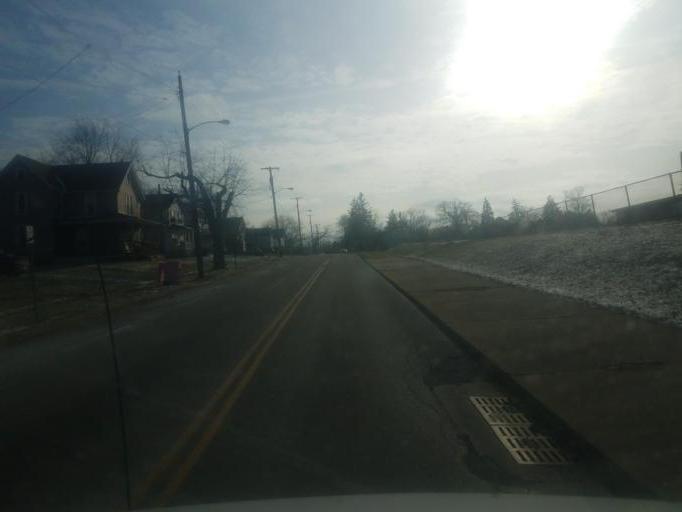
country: US
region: Ohio
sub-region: Richland County
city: Mansfield
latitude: 40.7536
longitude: -82.5100
